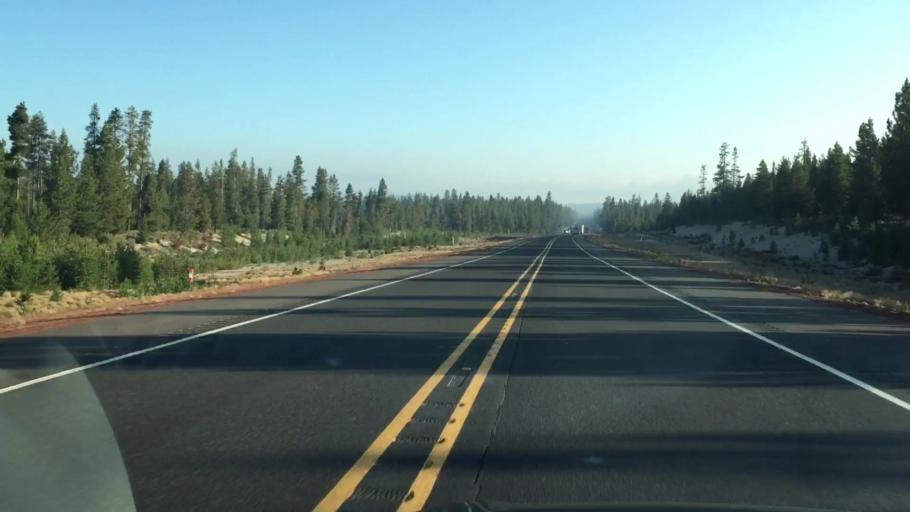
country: US
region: Oregon
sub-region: Deschutes County
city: La Pine
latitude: 43.2367
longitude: -121.7892
